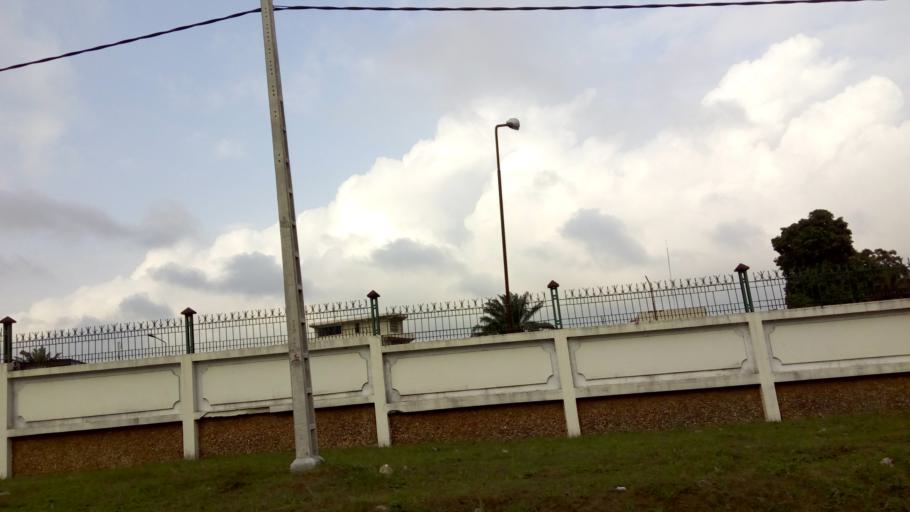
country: CI
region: Lagunes
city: Abidjan
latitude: 5.3359
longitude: -4.0253
